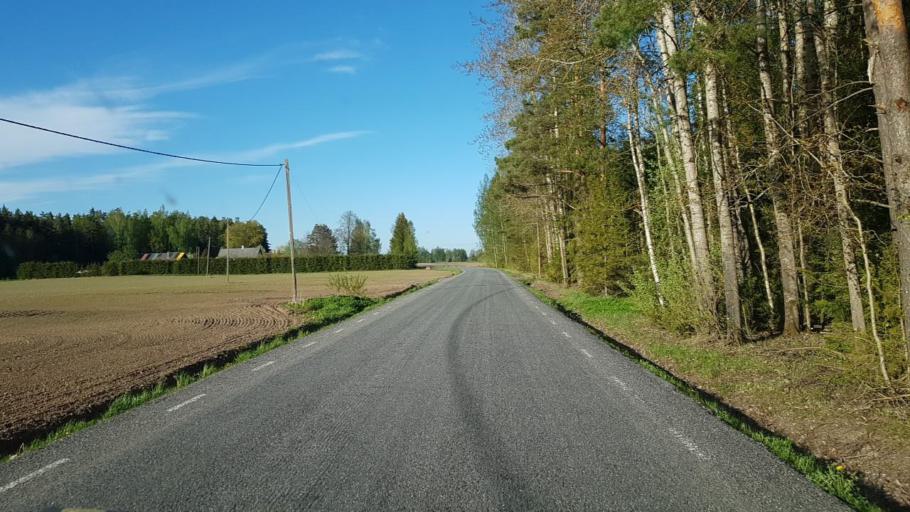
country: EE
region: Polvamaa
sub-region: Polva linn
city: Polva
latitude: 58.1274
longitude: 27.2561
